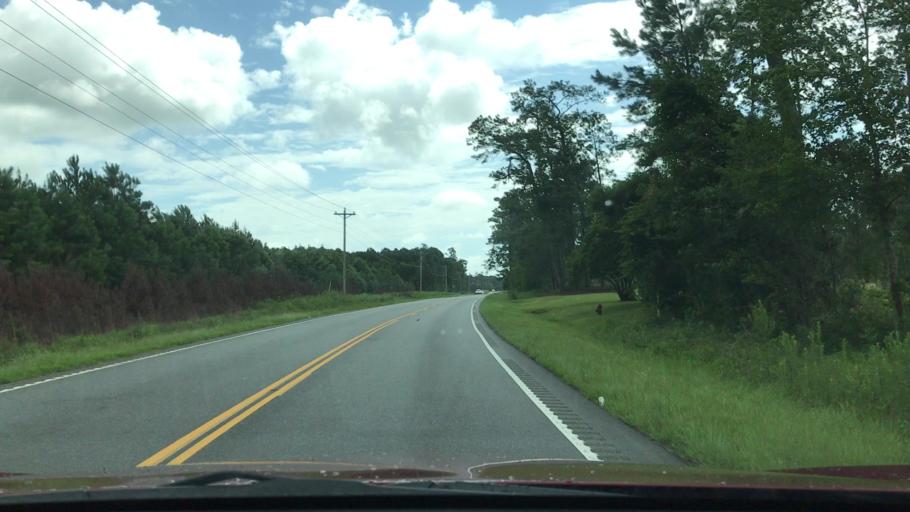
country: US
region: South Carolina
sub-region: Horry County
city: North Myrtle Beach
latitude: 33.9238
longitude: -78.7956
